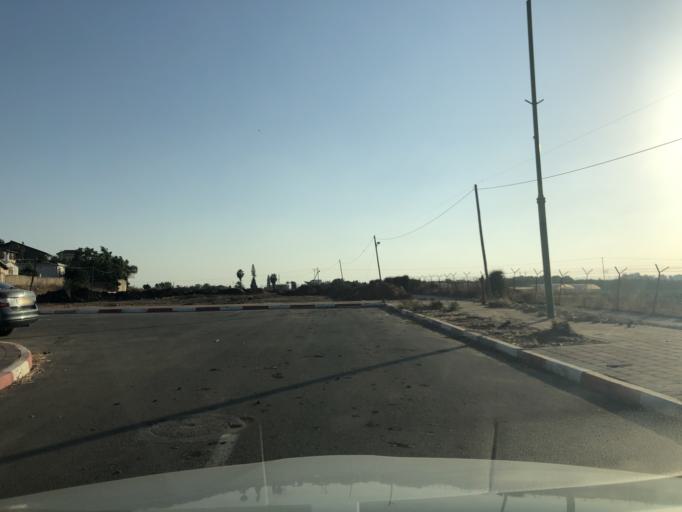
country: PS
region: West Bank
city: Hablah
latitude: 32.1572
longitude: 34.9699
